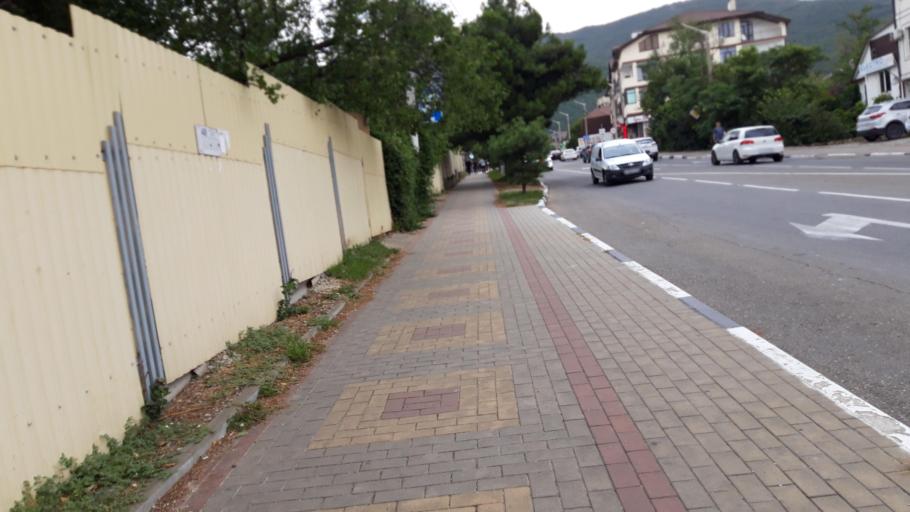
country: RU
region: Krasnodarskiy
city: Gelendzhik
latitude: 44.5659
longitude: 38.0876
